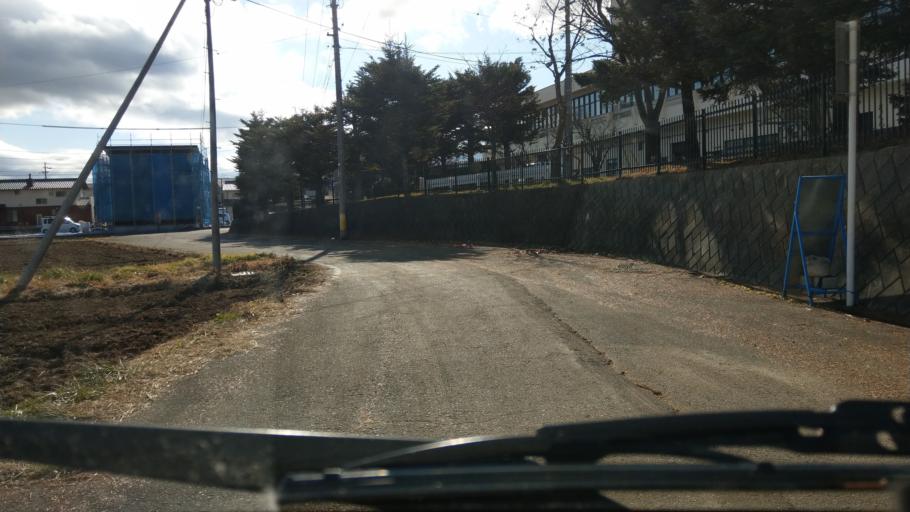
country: JP
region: Nagano
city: Saku
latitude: 36.2470
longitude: 138.4609
